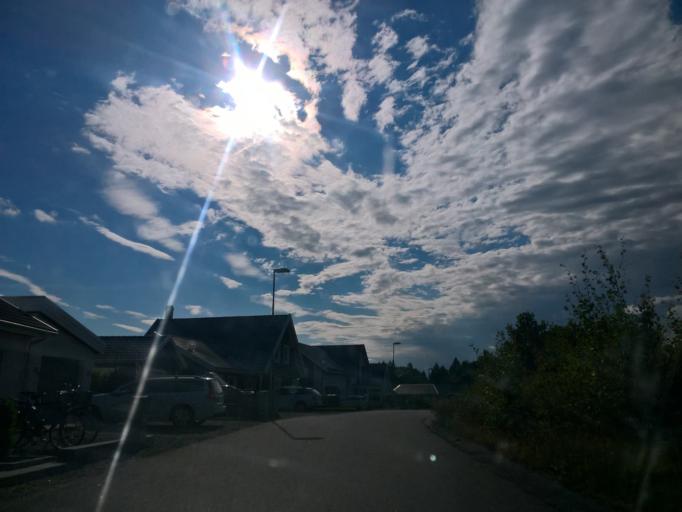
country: SE
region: OEstergoetland
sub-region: Finspangs Kommun
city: Finspang
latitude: 58.7066
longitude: 15.8288
